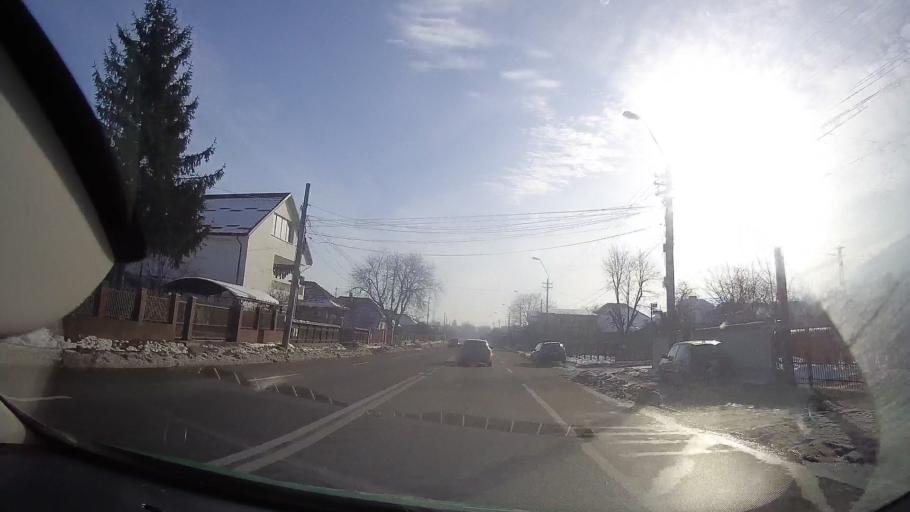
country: RO
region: Neamt
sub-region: Comuna Dobreni
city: Dobreni
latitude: 46.9529
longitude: 26.3838
